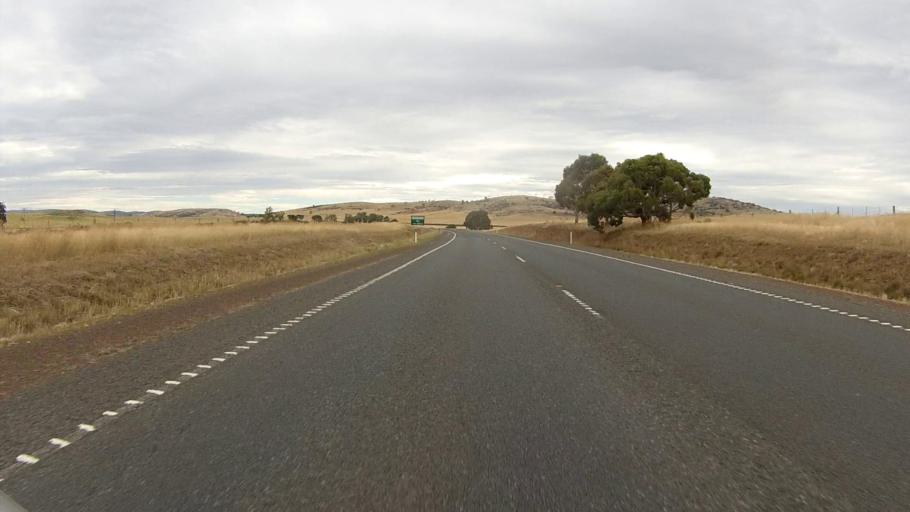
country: AU
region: Tasmania
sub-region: Brighton
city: Bridgewater
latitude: -42.3733
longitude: 147.3305
